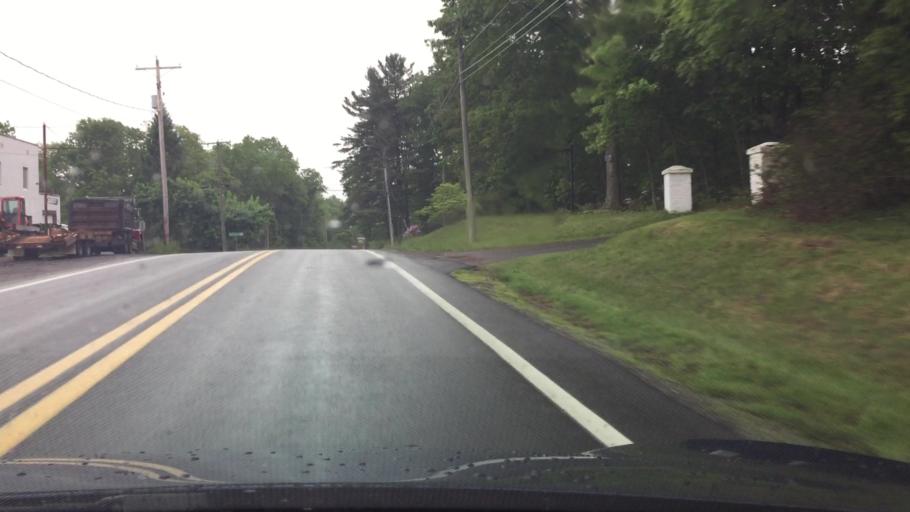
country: US
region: West Virginia
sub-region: Raleigh County
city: Shady Spring
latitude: 37.6910
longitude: -81.0631
